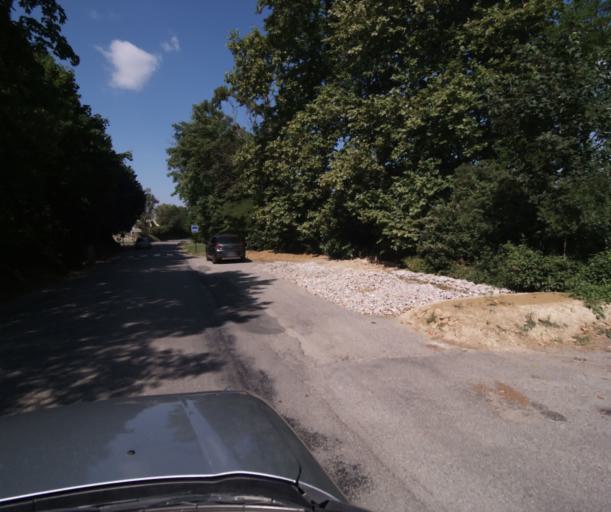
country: FR
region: Languedoc-Roussillon
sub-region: Departement de l'Aude
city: Limoux
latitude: 43.0528
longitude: 2.2068
